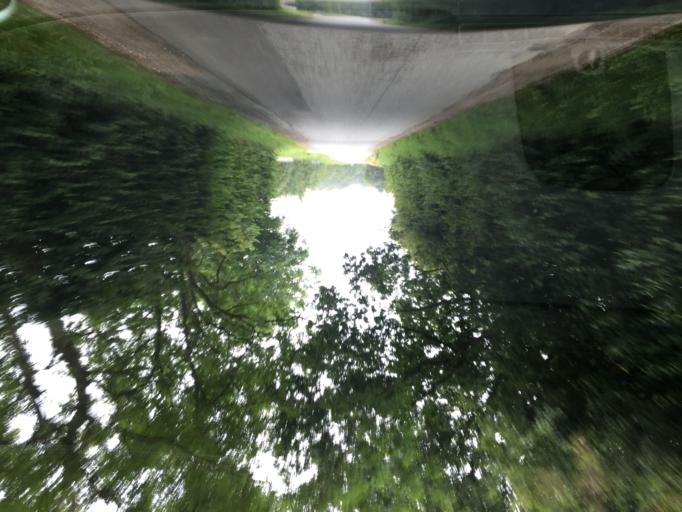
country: DK
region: South Denmark
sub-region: Kolding Kommune
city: Kolding
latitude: 55.5649
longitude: 9.4759
